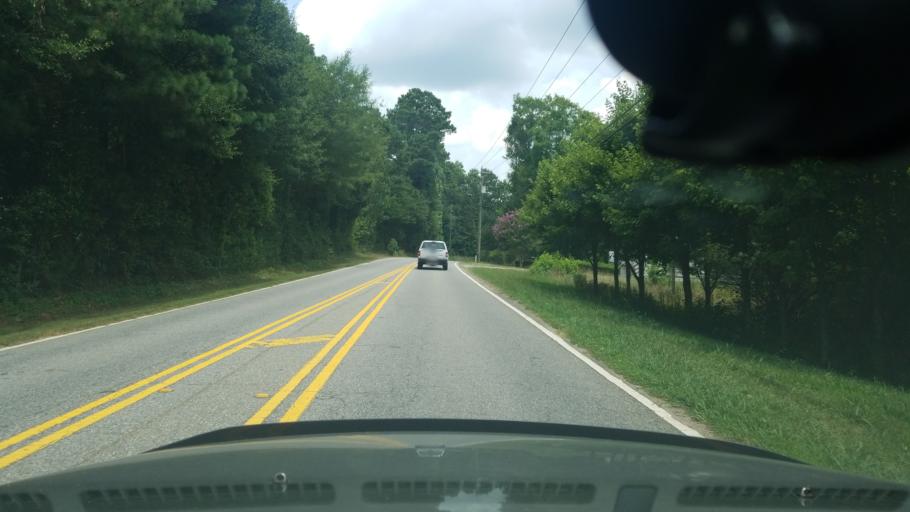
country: US
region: Georgia
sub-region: Fulton County
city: Milton
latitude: 34.1933
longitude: -84.2355
